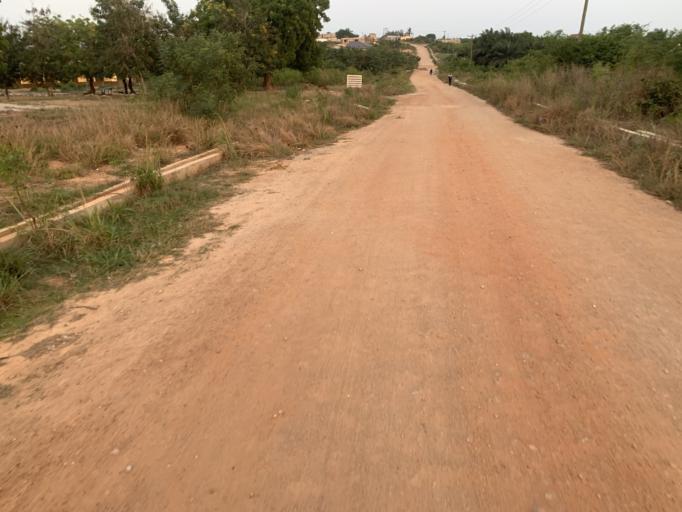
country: GH
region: Central
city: Winneba
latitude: 5.3769
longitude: -0.6108
